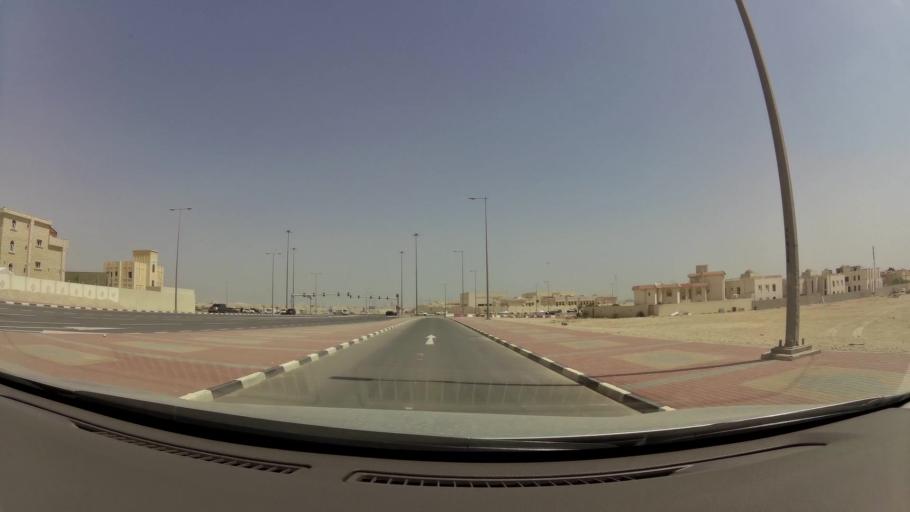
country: QA
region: Baladiyat Umm Salal
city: Umm Salal Muhammad
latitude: 25.4038
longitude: 51.4537
